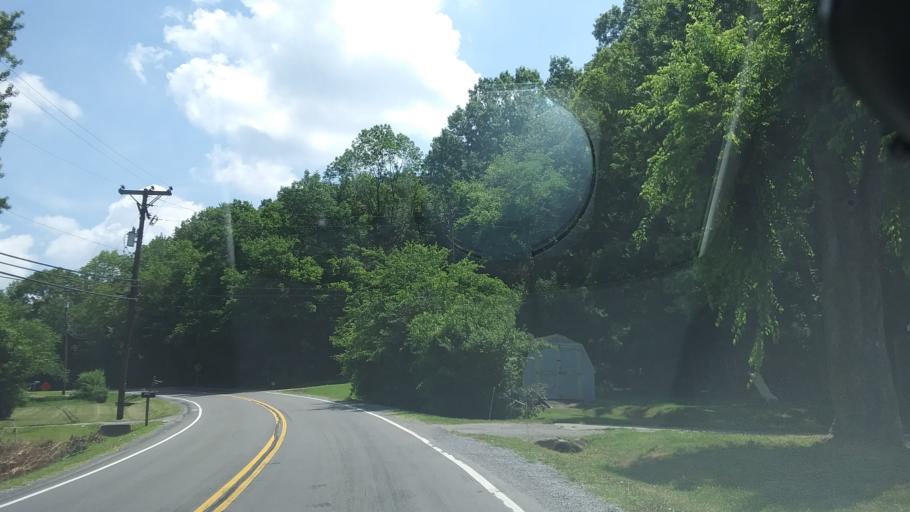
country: US
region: Tennessee
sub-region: Davidson County
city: Belle Meade
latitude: 36.0850
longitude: -86.9392
